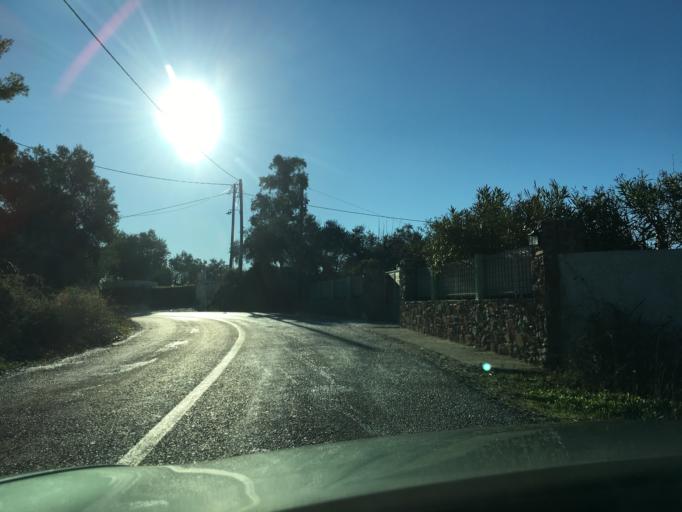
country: GR
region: Thessaly
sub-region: Nomos Magnisias
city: Skopelos
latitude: 39.0977
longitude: 23.6899
